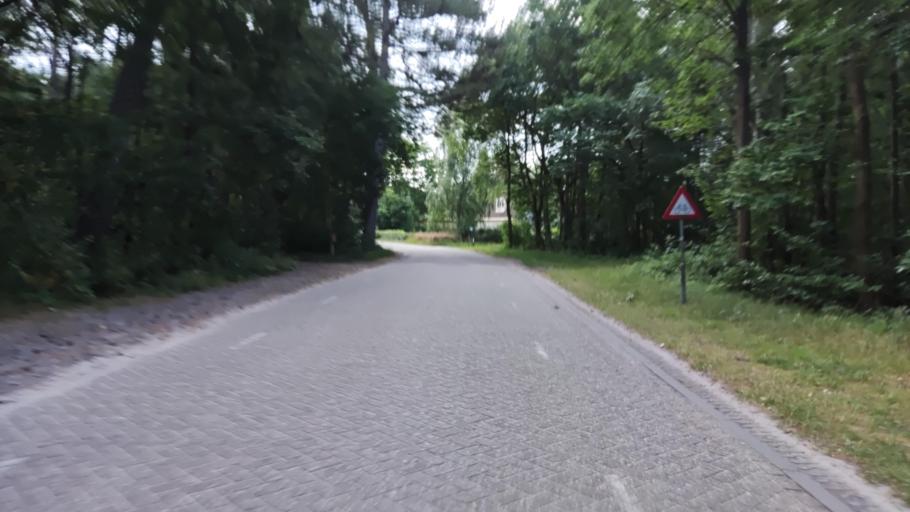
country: NL
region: North Holland
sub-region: Gemeente Texel
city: Den Burg
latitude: 53.0820
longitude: 4.7582
